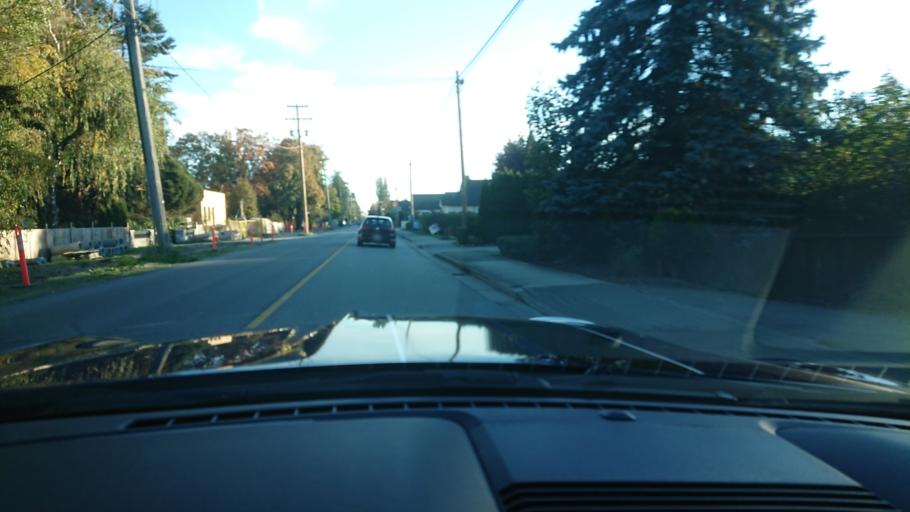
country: CA
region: British Columbia
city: Richmond
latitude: 49.1273
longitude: -123.1590
